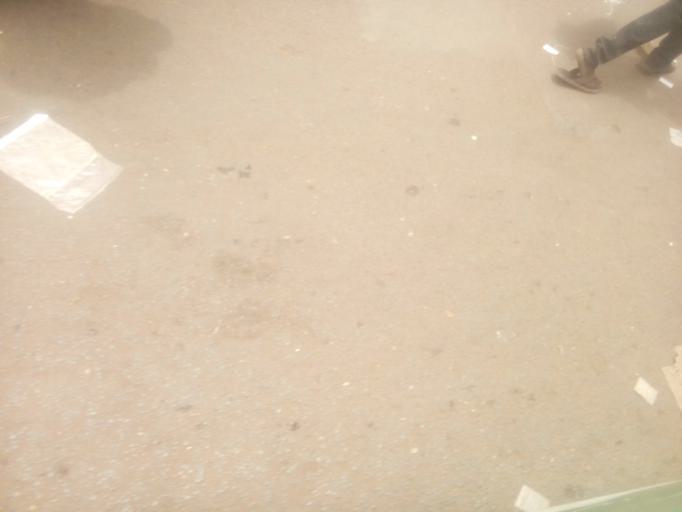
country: ML
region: Bamako
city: Bamako
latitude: 12.6478
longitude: -7.9940
